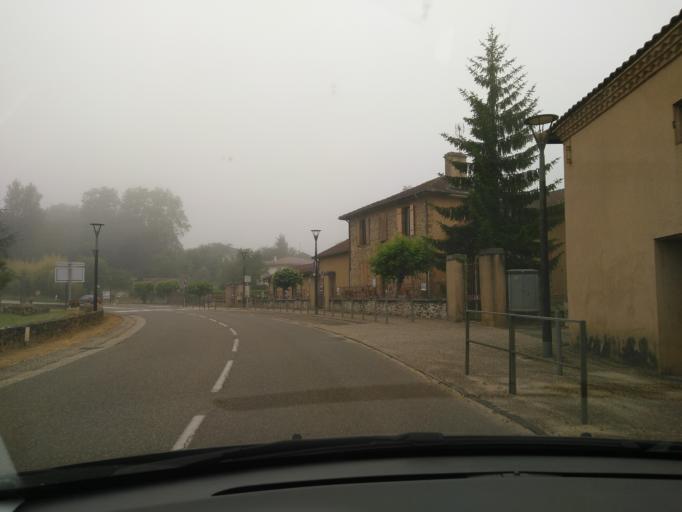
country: FR
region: Aquitaine
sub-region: Departement des Landes
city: Villeneuve-de-Marsan
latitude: 43.8899
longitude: -0.3919
